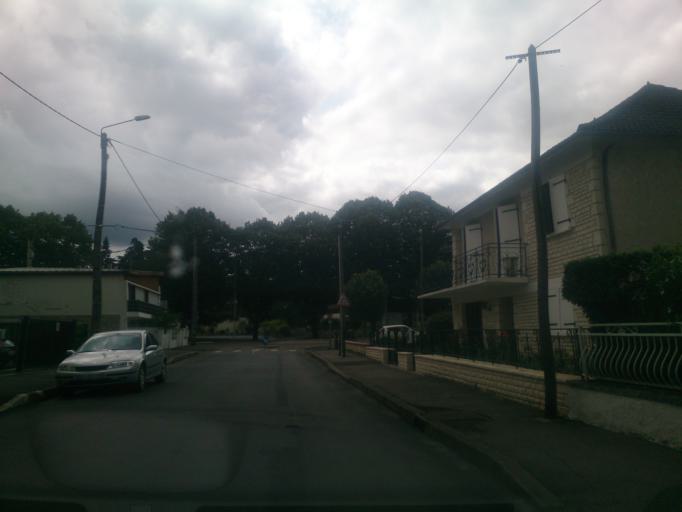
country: FR
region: Limousin
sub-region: Departement de la Correze
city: Brive-la-Gaillarde
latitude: 45.1600
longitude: 1.5428
